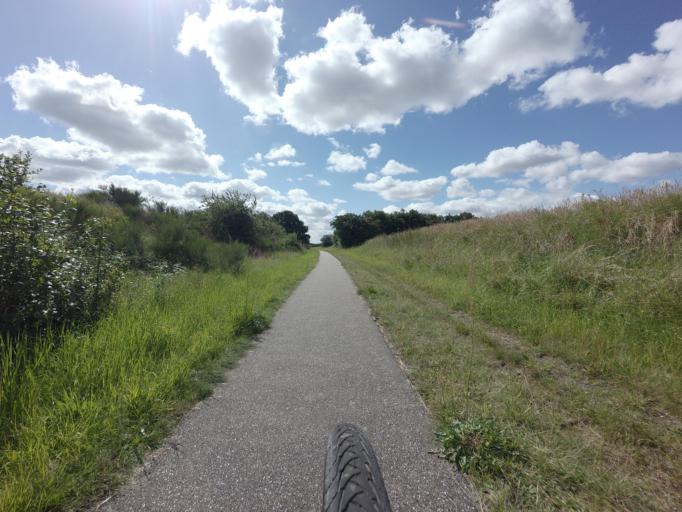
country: DK
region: Central Jutland
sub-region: Horsens Kommune
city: Horsens
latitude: 55.9197
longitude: 9.7674
